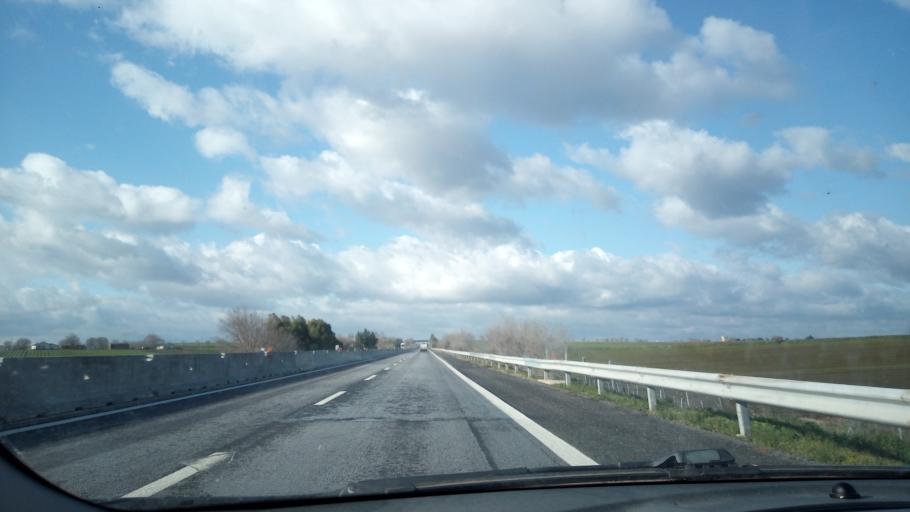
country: IT
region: Apulia
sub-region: Provincia di Foggia
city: Stornarella
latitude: 41.1790
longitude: 15.7321
